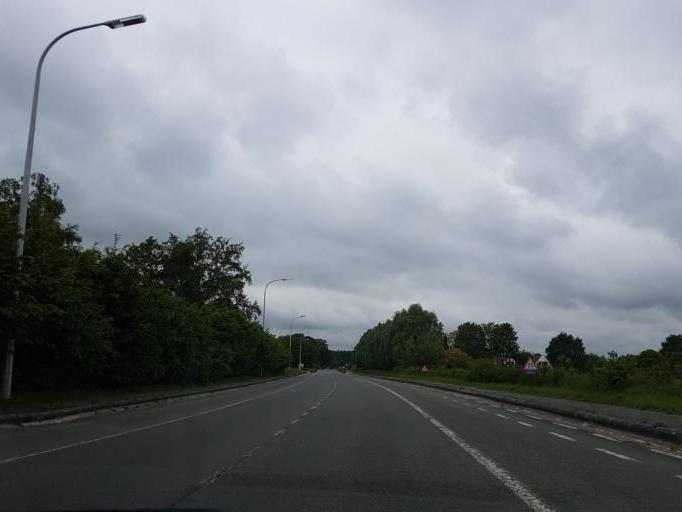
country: BE
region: Flanders
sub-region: Provincie Oost-Vlaanderen
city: Zomergem
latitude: 51.0971
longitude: 3.5731
